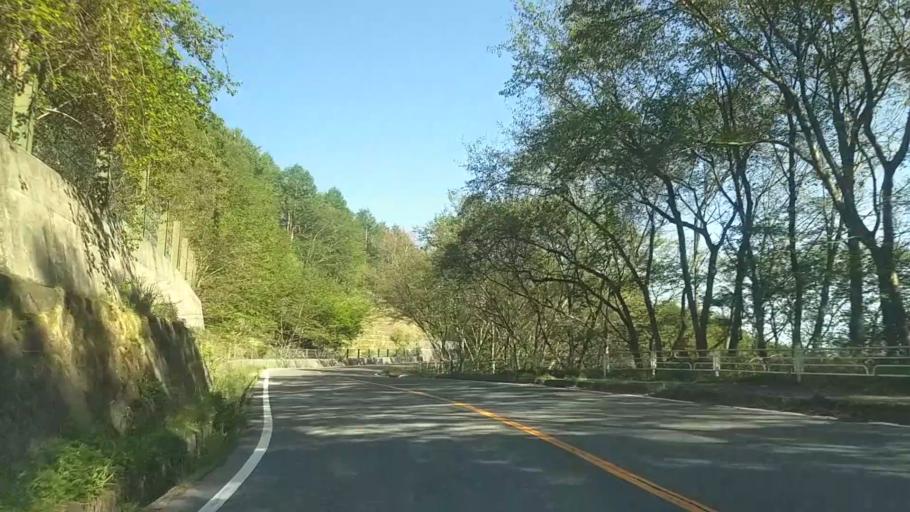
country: JP
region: Yamanashi
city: Nirasaki
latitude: 35.9034
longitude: 138.3822
